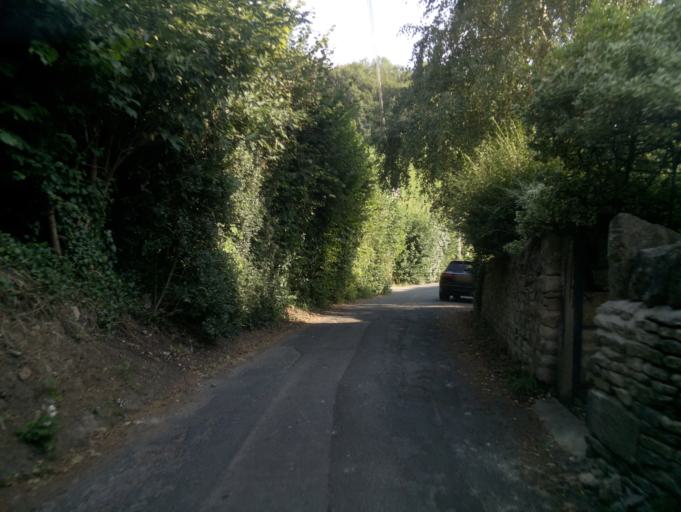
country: GB
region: England
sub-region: Gloucestershire
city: Stroud
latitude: 51.7334
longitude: -2.2262
